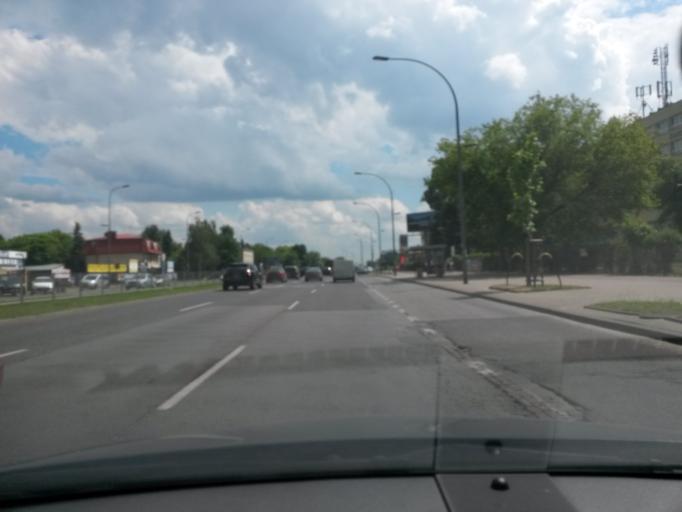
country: PL
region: Masovian Voivodeship
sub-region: Warszawa
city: Mokotow
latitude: 52.1901
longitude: 21.0600
